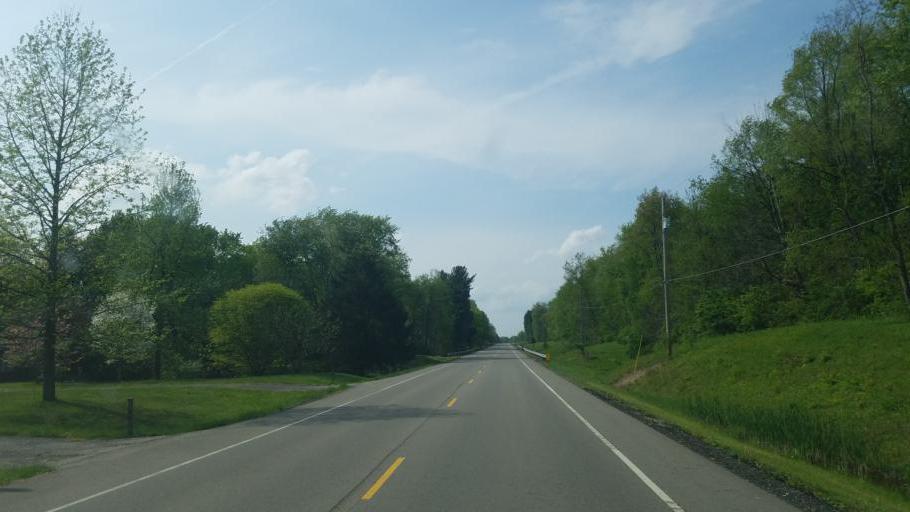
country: US
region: Ohio
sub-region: Licking County
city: Johnstown
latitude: 40.1069
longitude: -82.6411
